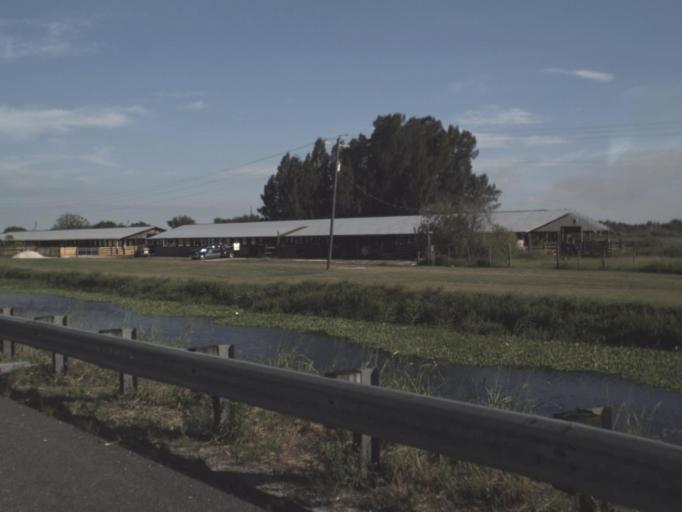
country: US
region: Florida
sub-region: Hendry County
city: Harlem
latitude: 26.7540
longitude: -80.9635
